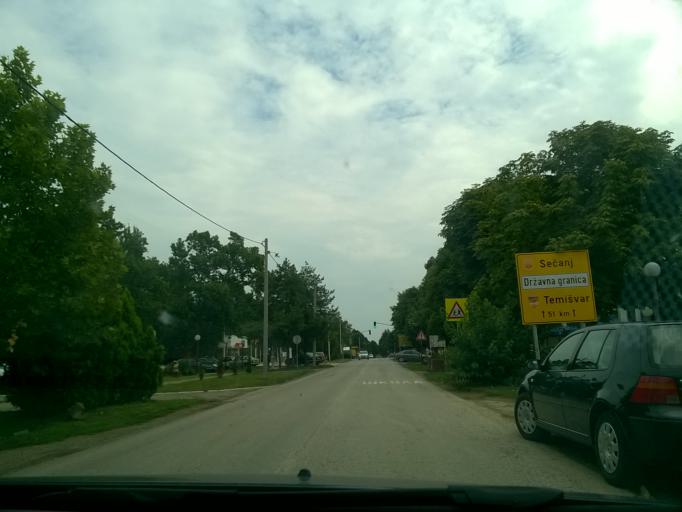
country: RS
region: Autonomna Pokrajina Vojvodina
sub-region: Srednjebanatski Okrug
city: Secanj
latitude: 45.3667
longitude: 20.7713
